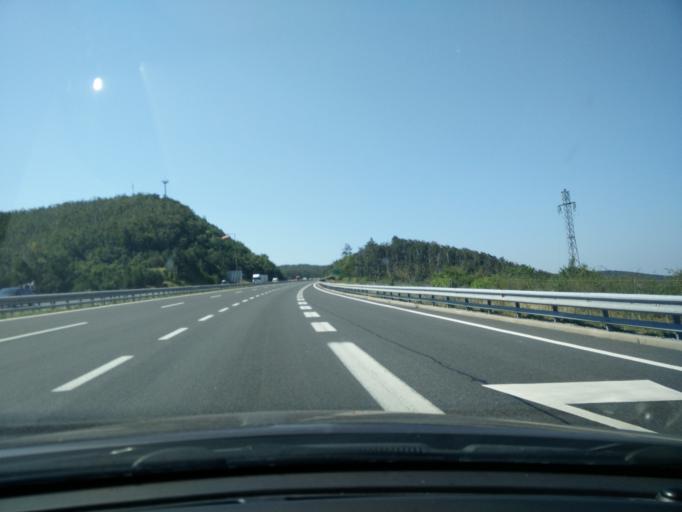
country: SI
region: Divaca
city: Divaca
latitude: 45.7556
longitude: 14.0511
